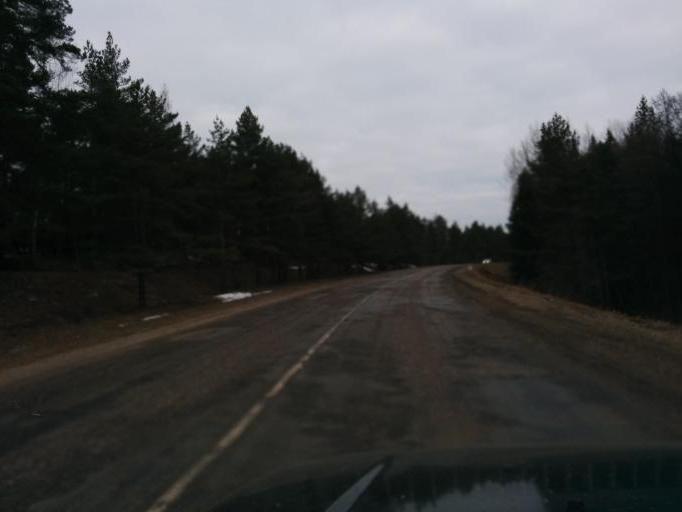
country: LV
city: Tireli
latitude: 56.8822
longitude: 23.5348
